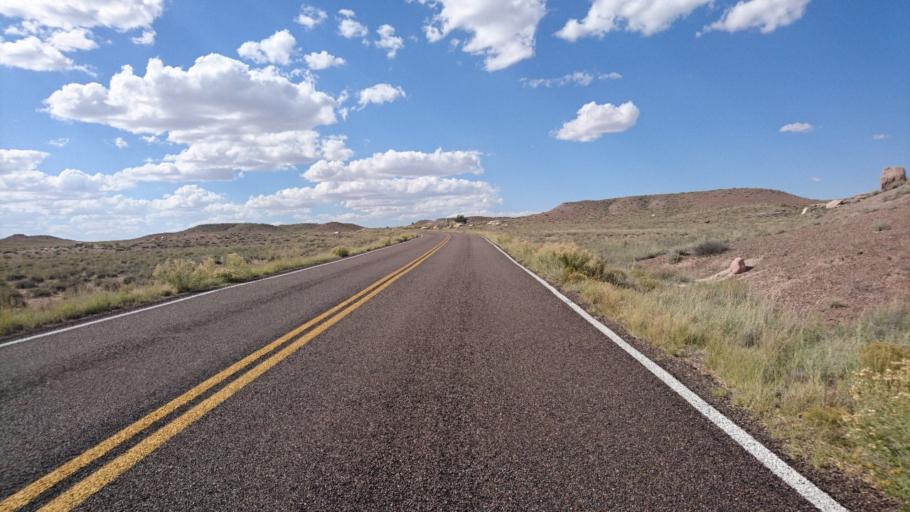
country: US
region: Arizona
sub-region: Navajo County
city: Holbrook
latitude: 34.8873
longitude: -109.8044
